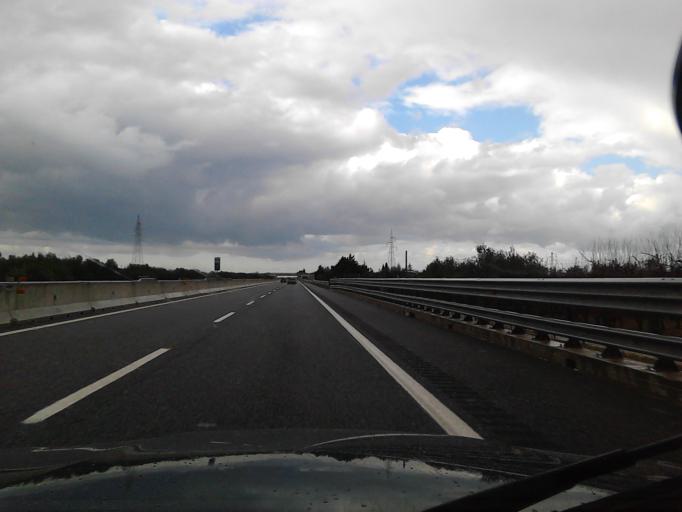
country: IT
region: Apulia
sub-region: Provincia di Bari
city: Molfetta
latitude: 41.1667
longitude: 16.6147
